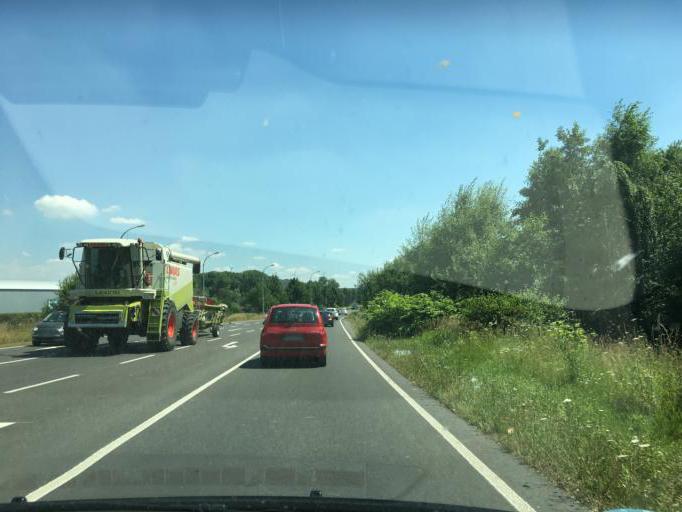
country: DE
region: North Rhine-Westphalia
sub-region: Regierungsbezirk Koln
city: Eschweiler
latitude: 50.8210
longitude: 6.3015
